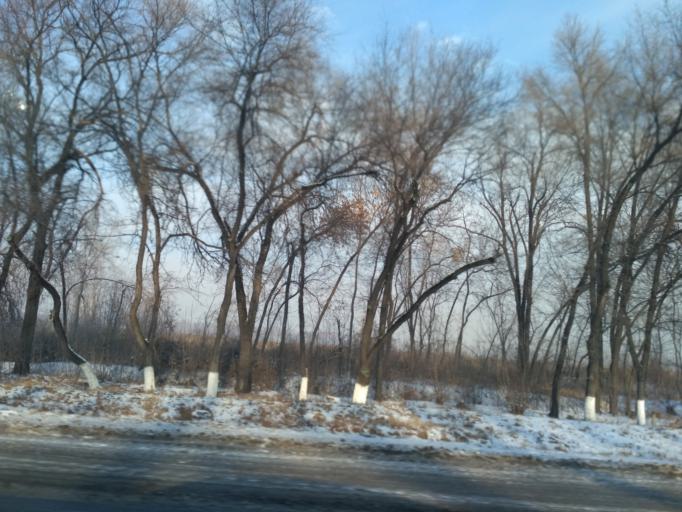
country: KZ
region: Almaty Oblysy
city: Burunday
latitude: 43.2206
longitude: 76.7138
